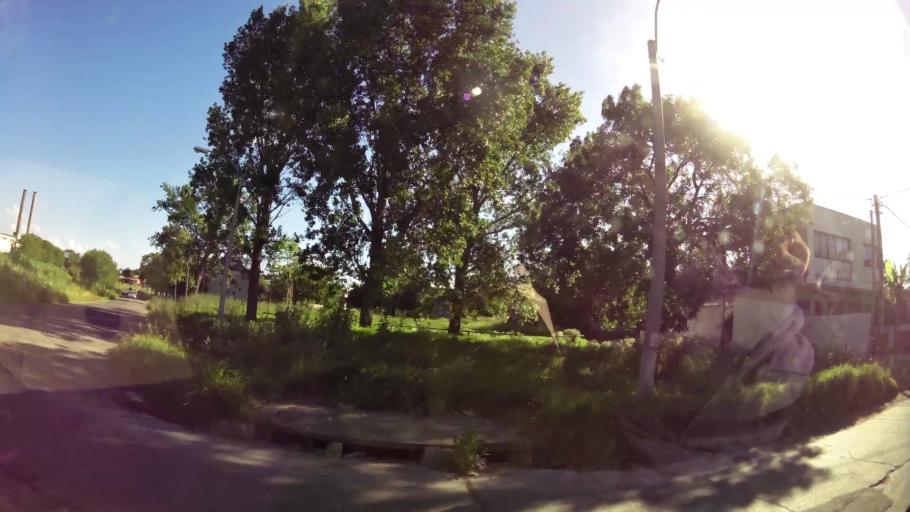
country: UY
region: Montevideo
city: Montevideo
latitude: -34.8487
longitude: -56.2169
